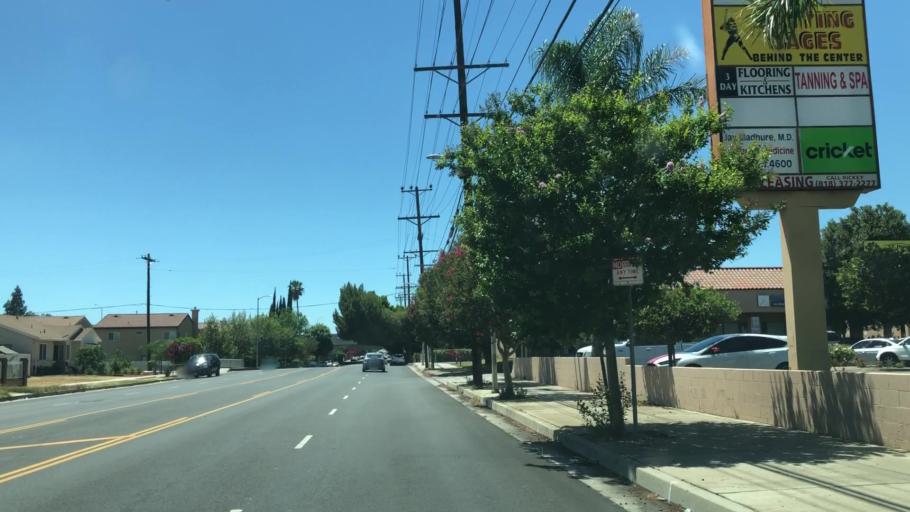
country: US
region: California
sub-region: Los Angeles County
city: San Fernando
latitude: 34.2720
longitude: -118.4859
